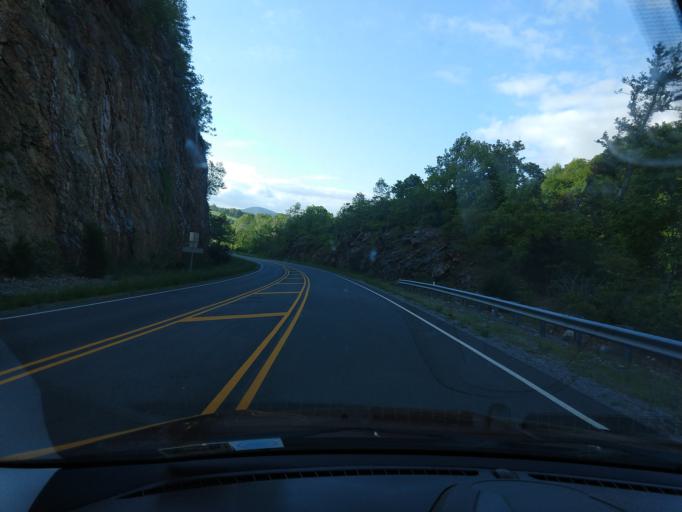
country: US
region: Virginia
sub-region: Wythe County
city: Wytheville
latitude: 36.8516
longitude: -80.9763
